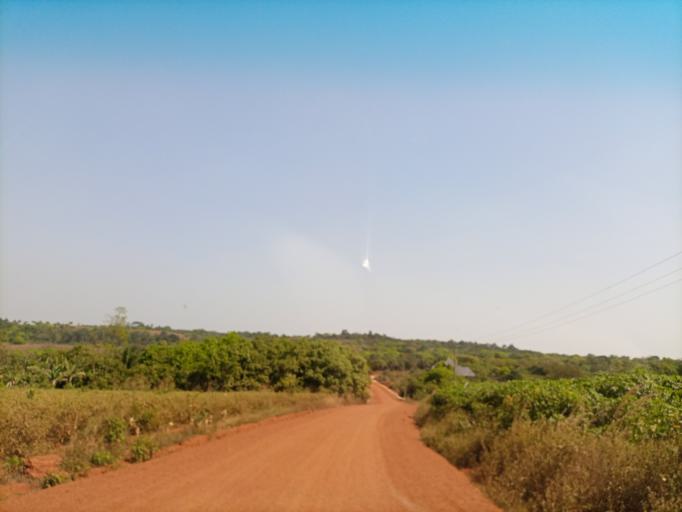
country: NG
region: Enugu
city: Nsukka
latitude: 6.8014
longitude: 7.3391
